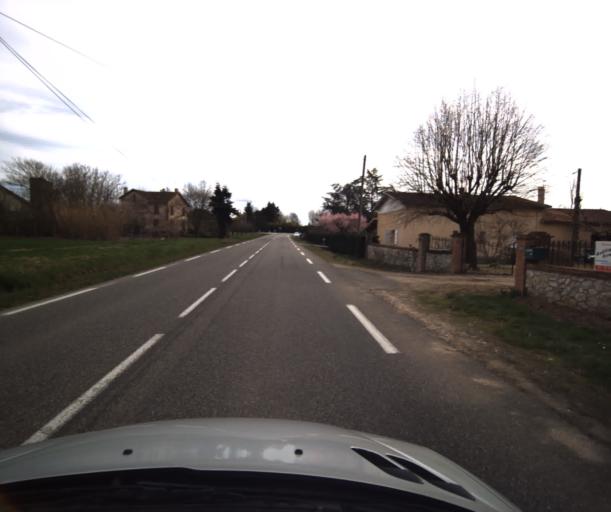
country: FR
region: Midi-Pyrenees
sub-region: Departement du Tarn-et-Garonne
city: Montbeton
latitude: 44.0721
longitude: 1.2853
